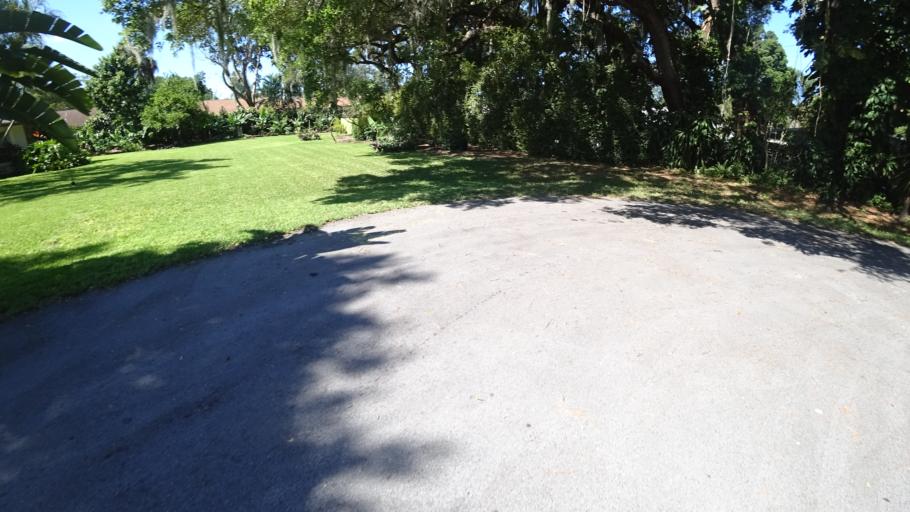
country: US
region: Florida
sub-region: Manatee County
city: South Bradenton
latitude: 27.4760
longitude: -82.6060
